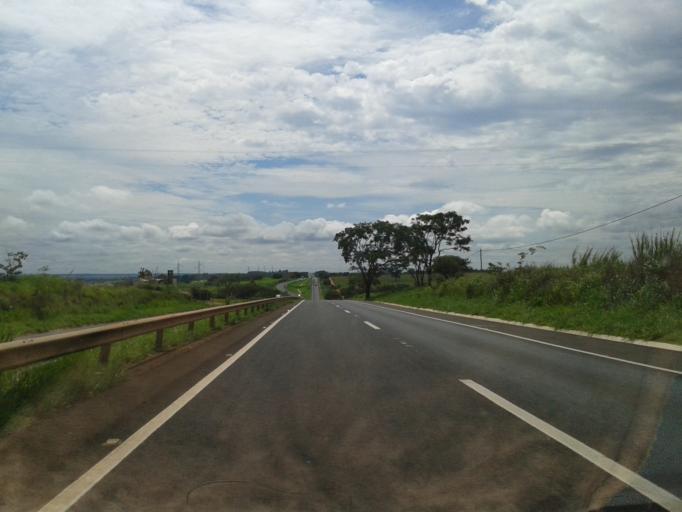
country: BR
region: Minas Gerais
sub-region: Tupaciguara
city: Tupaciguara
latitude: -18.8658
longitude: -48.5770
